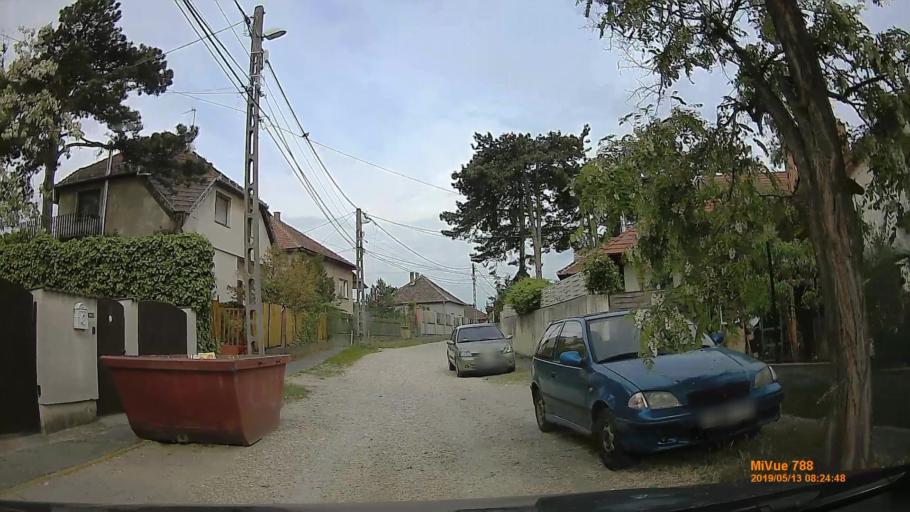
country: HU
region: Budapest
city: Budapest XXIII. keruelet
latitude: 47.4081
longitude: 19.0946
